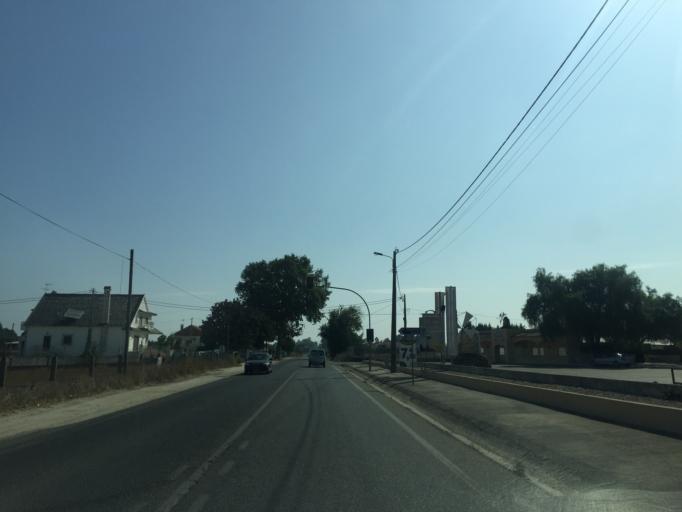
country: PT
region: Santarem
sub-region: Salvaterra de Magos
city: Salvaterra de Magos
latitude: 39.0265
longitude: -8.7820
